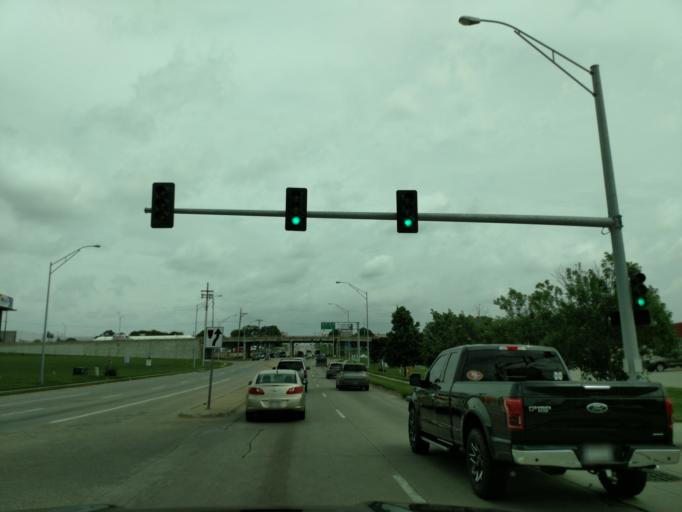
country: US
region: Nebraska
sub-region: Douglas County
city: Ralston
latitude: 41.2107
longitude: -96.0238
